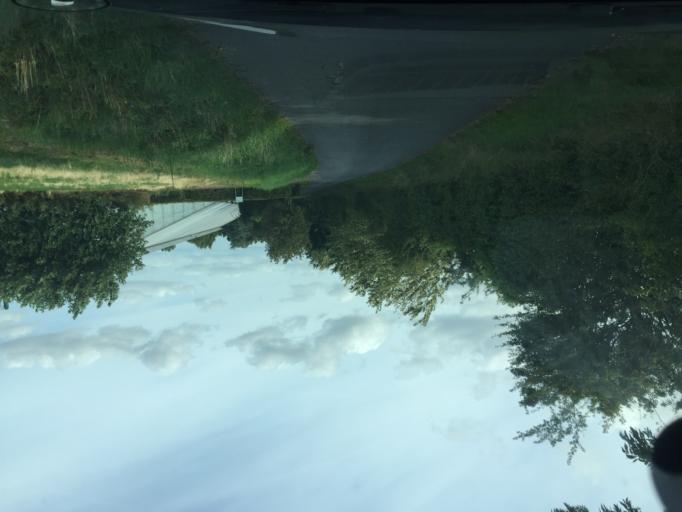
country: DK
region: South Denmark
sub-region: Faaborg-Midtfyn Kommune
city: Arslev
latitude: 55.3445
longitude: 10.5132
